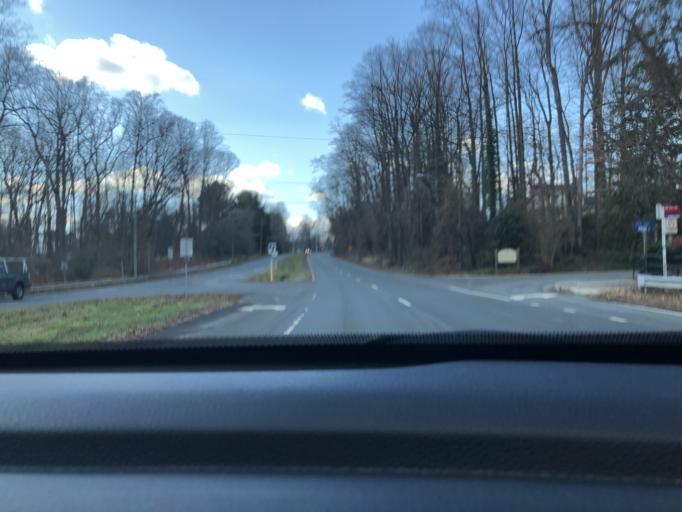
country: US
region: Virginia
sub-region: Fairfax County
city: Kings Park
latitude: 38.8109
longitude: -77.2575
